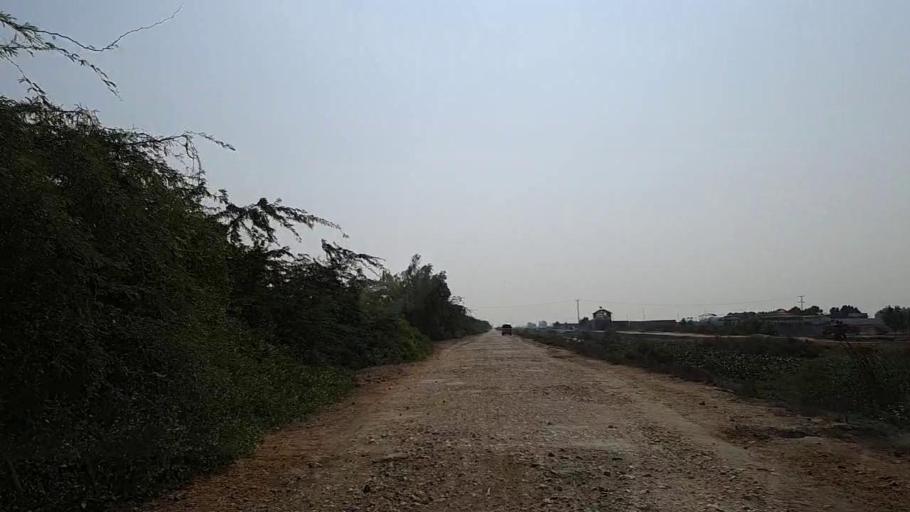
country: PK
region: Sindh
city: Thatta
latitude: 24.7223
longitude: 67.7684
